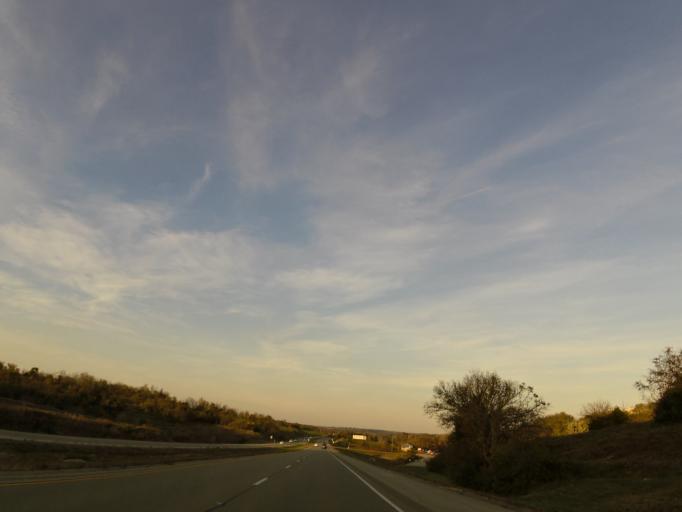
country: US
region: Kentucky
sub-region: Garrard County
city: Lancaster
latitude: 37.7347
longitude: -84.6355
